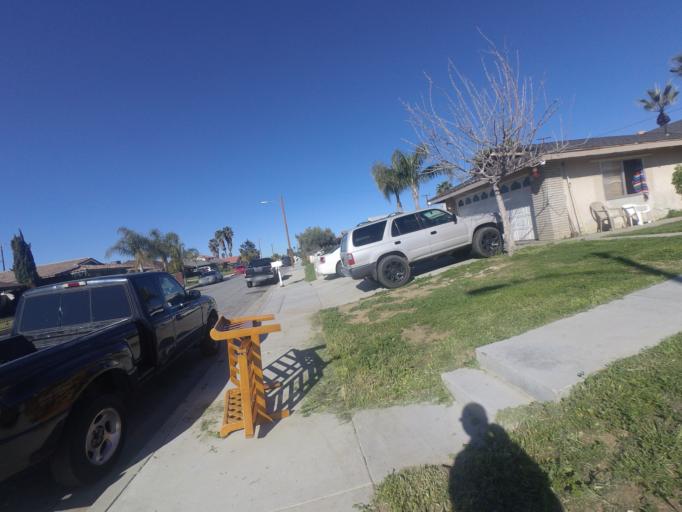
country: US
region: California
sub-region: Riverside County
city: March Air Force Base
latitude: 33.9237
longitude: -117.2668
